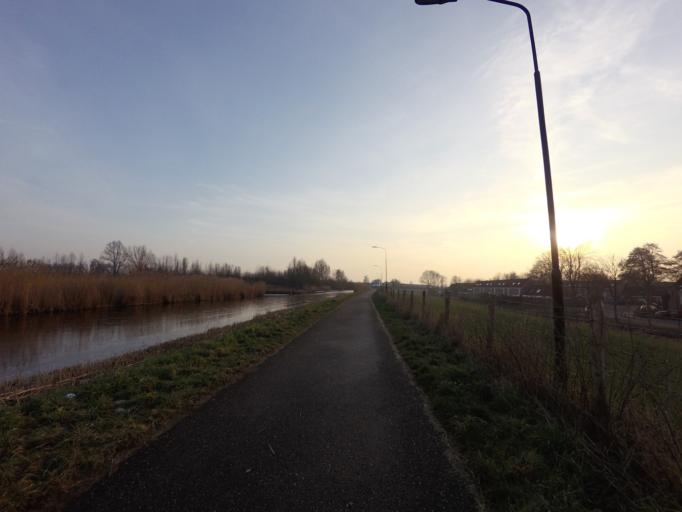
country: NL
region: Utrecht
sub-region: Gemeente De Ronde Venen
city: Mijdrecht
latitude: 52.2098
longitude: 4.9289
